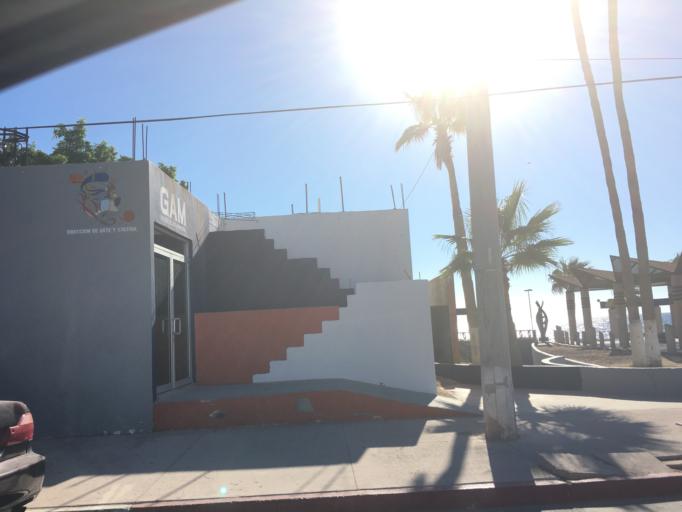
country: MX
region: Sonora
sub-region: Puerto Penasco
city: Puerto Penasco
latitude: 31.3020
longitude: -113.5506
